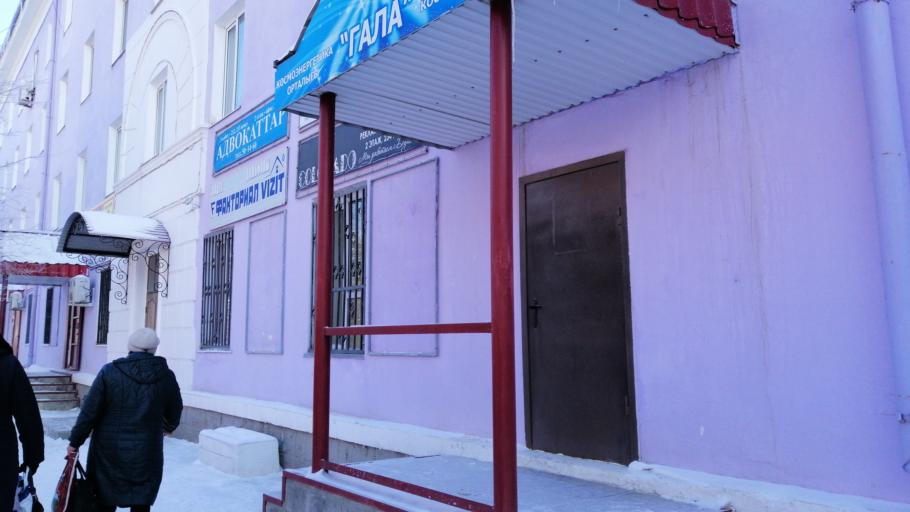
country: KZ
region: Aqtoebe
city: Aqtobe
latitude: 50.3107
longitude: 57.1472
